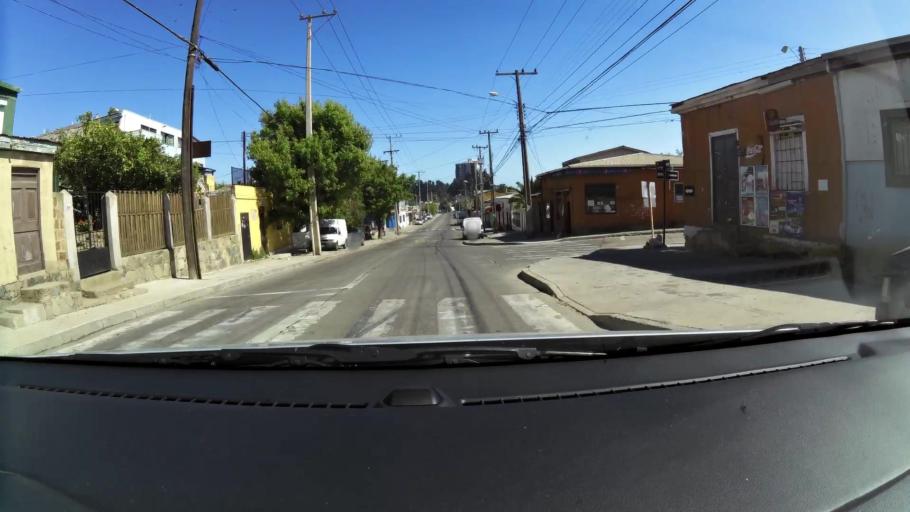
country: CL
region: Valparaiso
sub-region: Provincia de Valparaiso
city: Valparaiso
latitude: -33.0653
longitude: -71.5850
